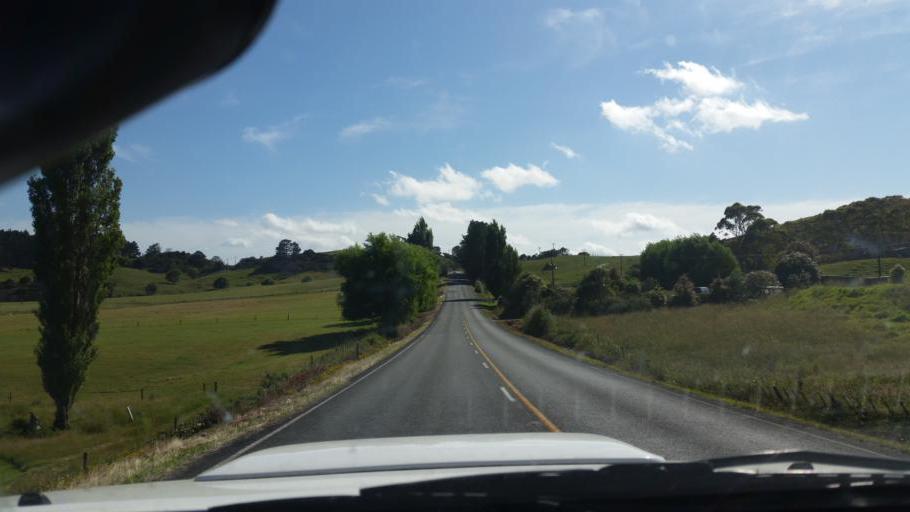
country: NZ
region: Northland
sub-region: Whangarei
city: Ruakaka
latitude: -36.1166
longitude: 174.2050
